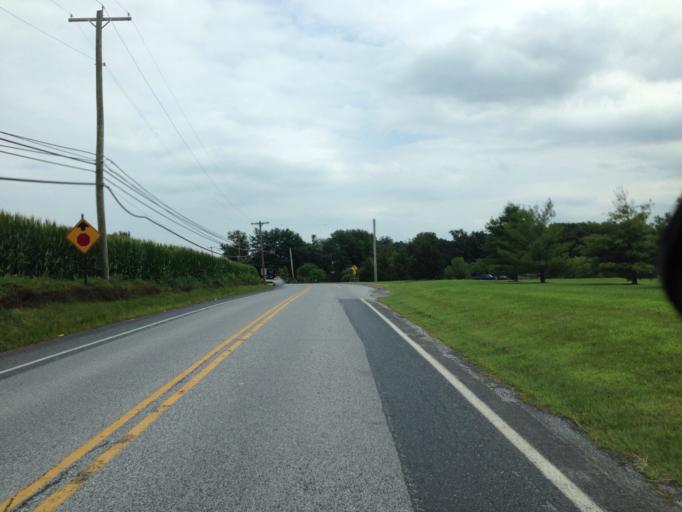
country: US
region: Pennsylvania
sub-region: Chester County
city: West Grove
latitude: 39.7435
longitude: -75.8069
